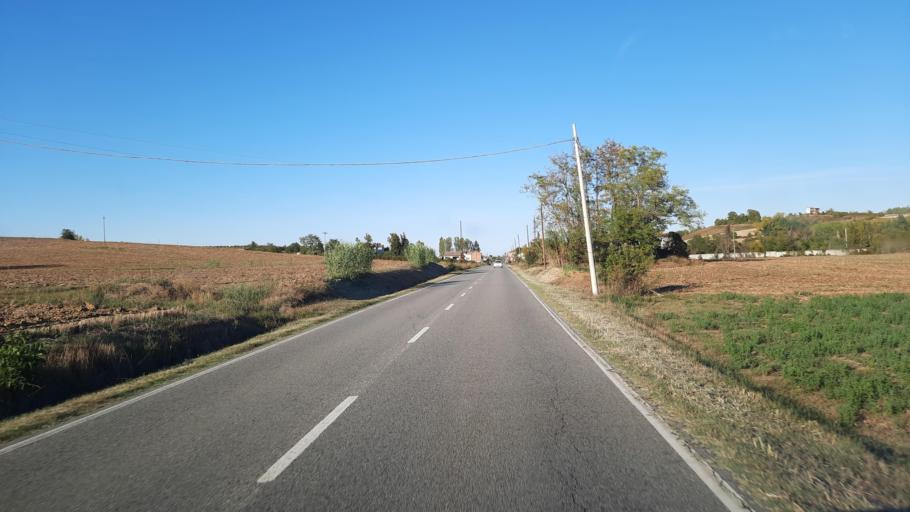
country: IT
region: Piedmont
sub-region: Provincia di Alessandria
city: Camagna Monferrato
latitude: 45.0294
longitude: 8.4169
